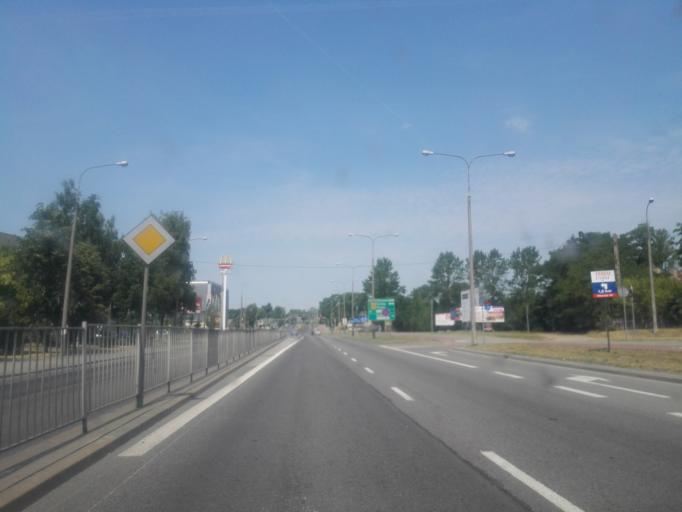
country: PL
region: Podlasie
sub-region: Suwalki
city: Suwalki
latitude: 54.1057
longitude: 22.9372
